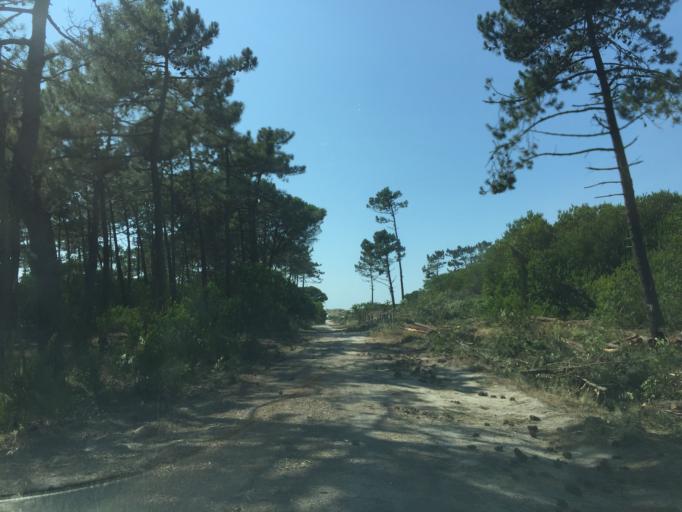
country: PT
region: Coimbra
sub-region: Figueira da Foz
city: Tavarede
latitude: 40.2635
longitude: -8.8637
